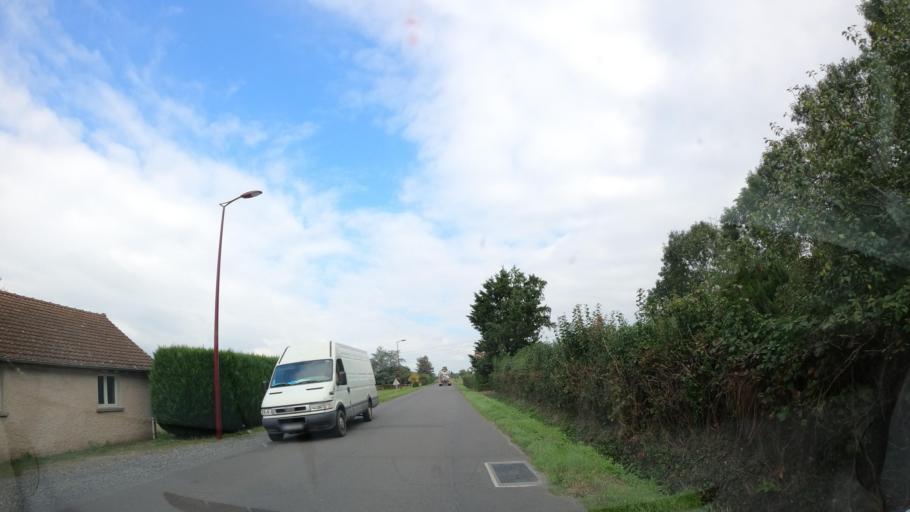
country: FR
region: Auvergne
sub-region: Departement de l'Allier
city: Saint-Gerand-le-Puy
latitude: 46.2154
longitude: 3.5088
